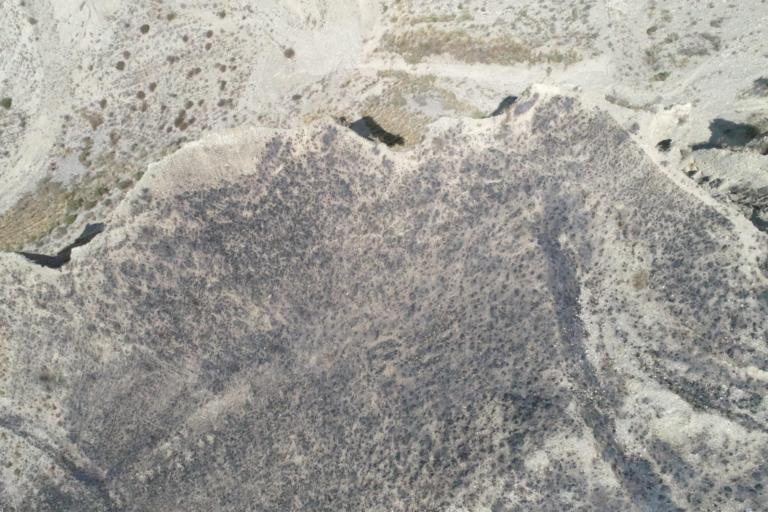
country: BO
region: La Paz
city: La Paz
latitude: -16.4709
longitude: -68.0976
